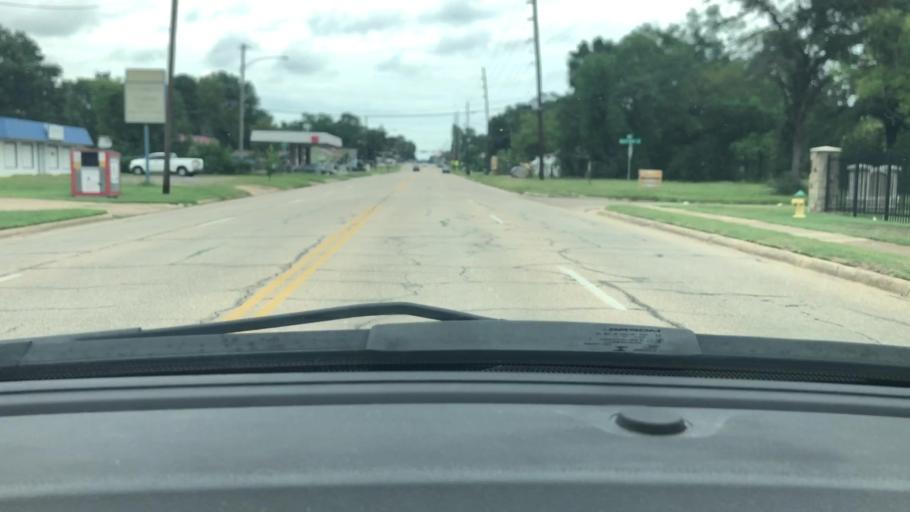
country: US
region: Texas
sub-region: Bowie County
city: Wake Village
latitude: 33.4280
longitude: -94.0804
